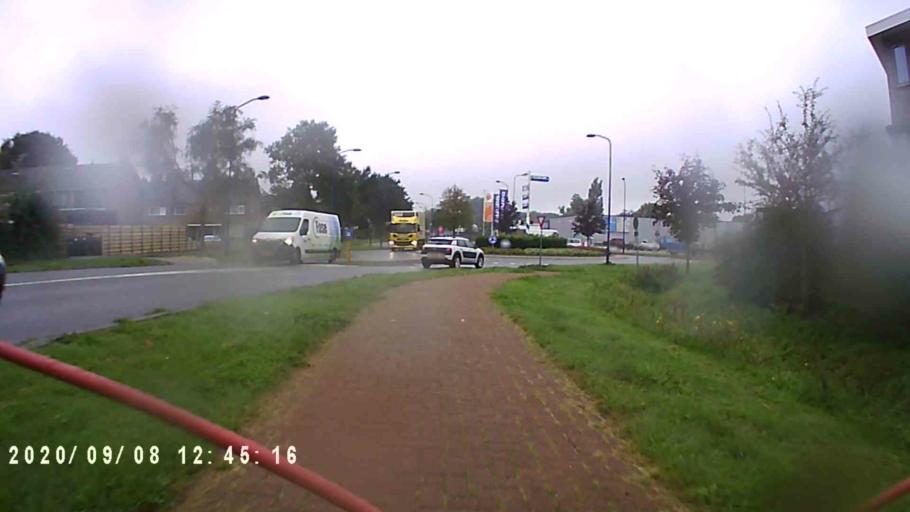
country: NL
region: Groningen
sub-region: Gemeente Veendam
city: Veendam
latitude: 53.1094
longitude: 6.8901
